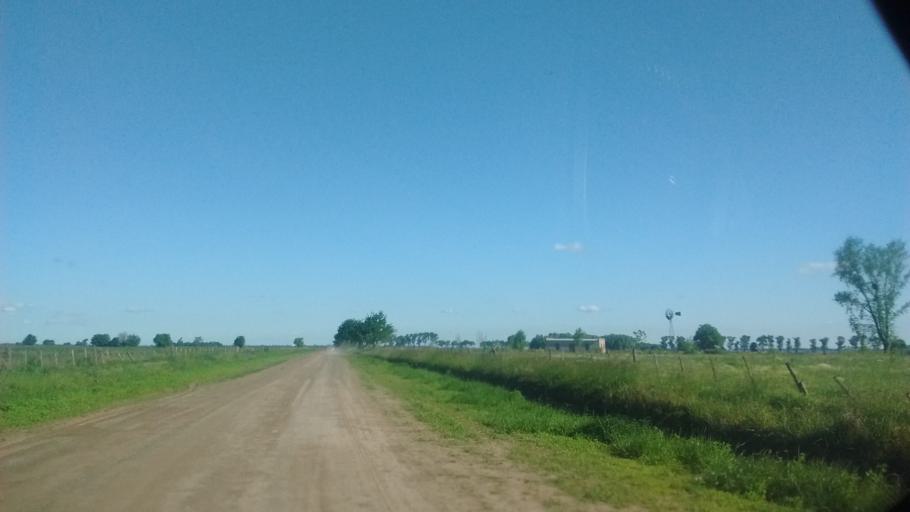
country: AR
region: Santa Fe
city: Funes
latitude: -32.8642
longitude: -60.8017
